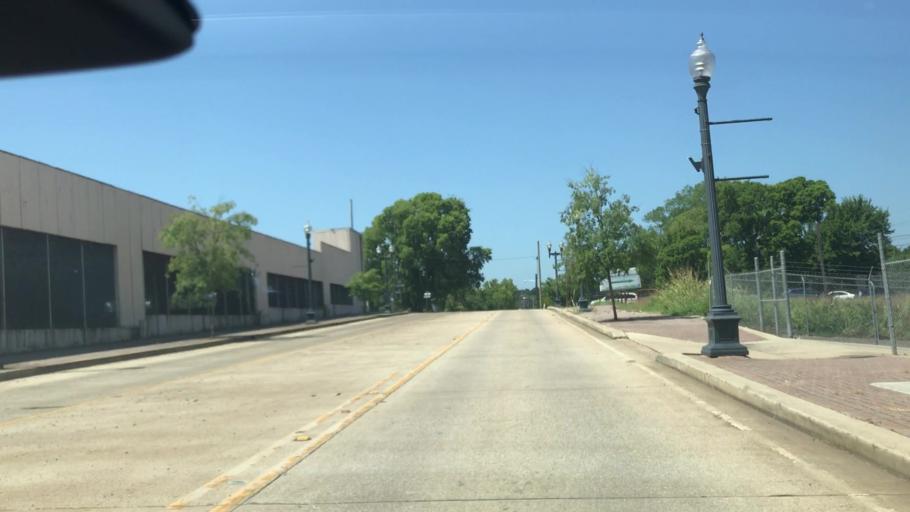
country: US
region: Louisiana
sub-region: Caddo Parish
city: Shreveport
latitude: 32.5152
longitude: -93.7524
